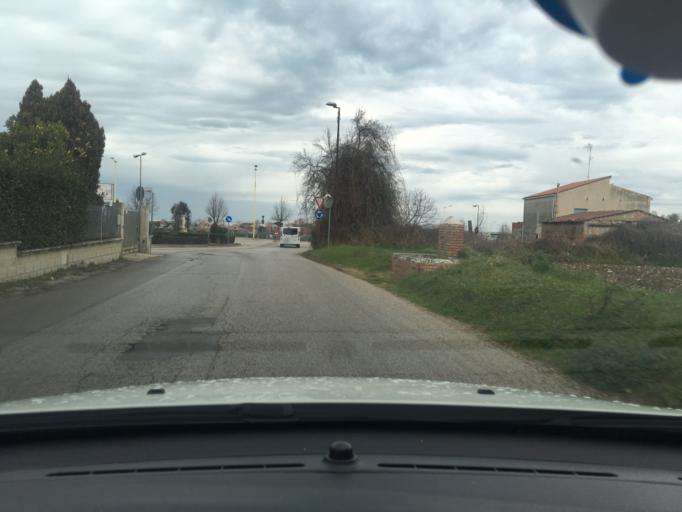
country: IT
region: Molise
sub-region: Provincia di Campobasso
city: Termoli
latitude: 41.9810
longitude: 14.9996
